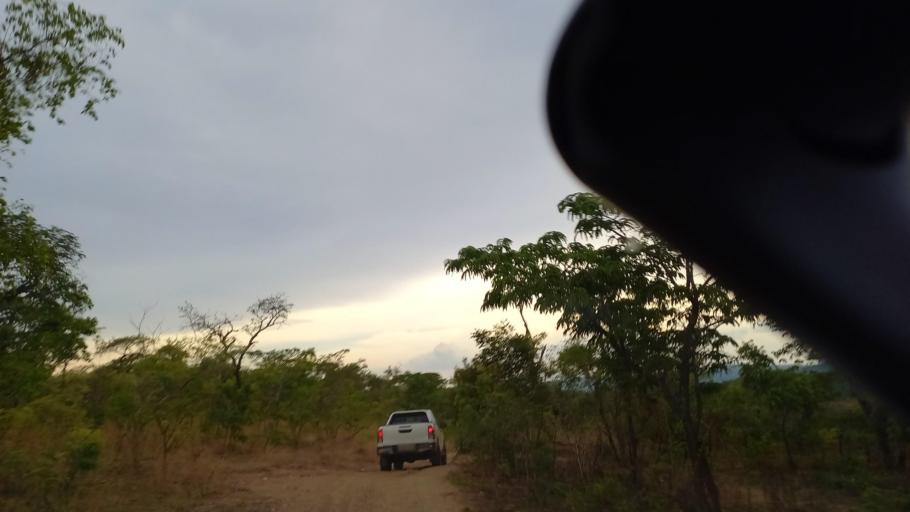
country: ZM
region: Lusaka
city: Kafue
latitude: -16.0519
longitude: 28.3371
